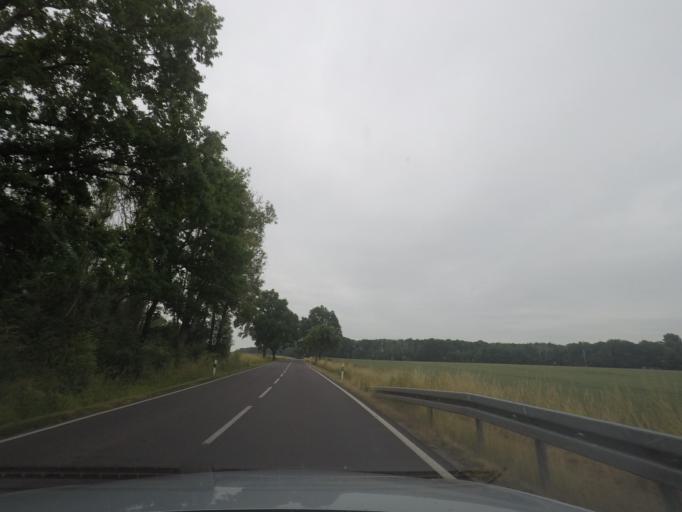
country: DE
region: Saxony-Anhalt
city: Seehausen
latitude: 52.0792
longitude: 11.2834
